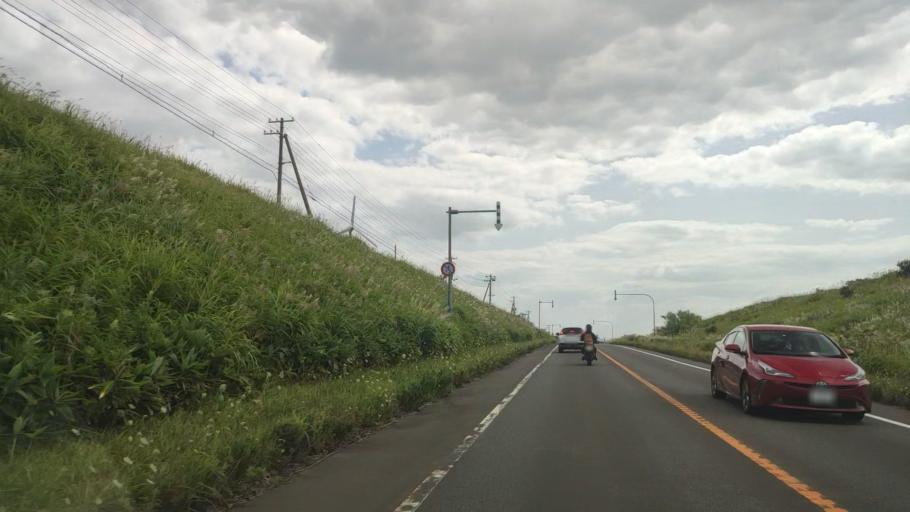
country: JP
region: Hokkaido
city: Rumoi
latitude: 44.5158
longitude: 141.7662
